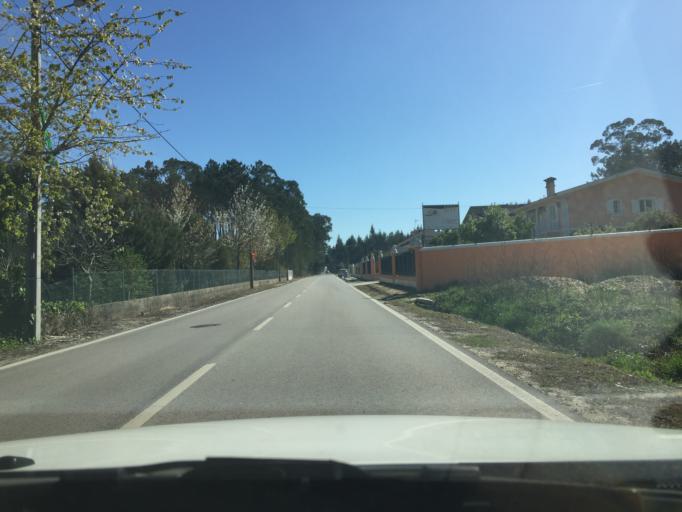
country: PT
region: Coimbra
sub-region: Cantanhede
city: Cantanhede
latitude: 40.4187
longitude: -8.5563
